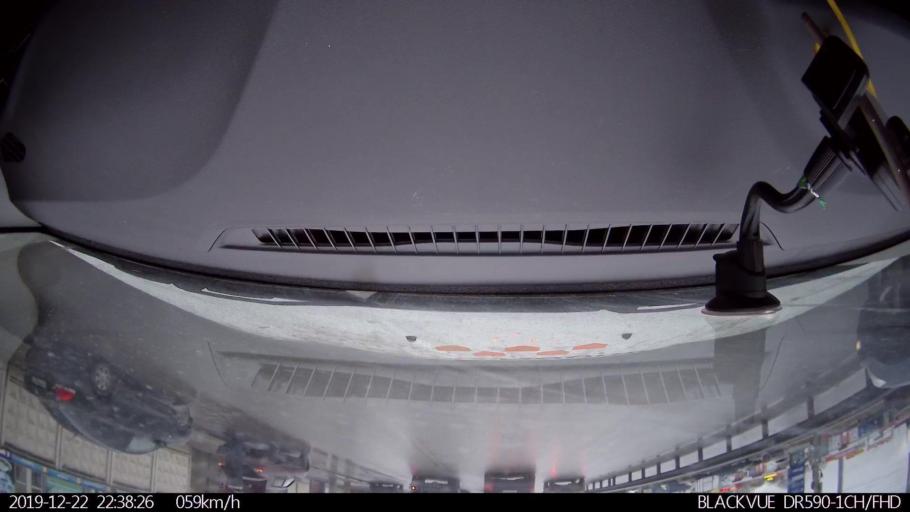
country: RU
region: Nizjnij Novgorod
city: Nizhniy Novgorod
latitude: 56.3059
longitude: 43.8713
